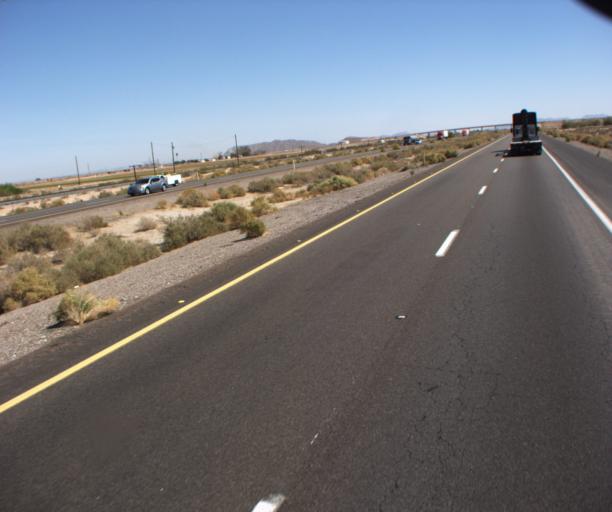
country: US
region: Arizona
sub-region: Yuma County
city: Wellton
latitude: 32.6734
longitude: -114.0840
